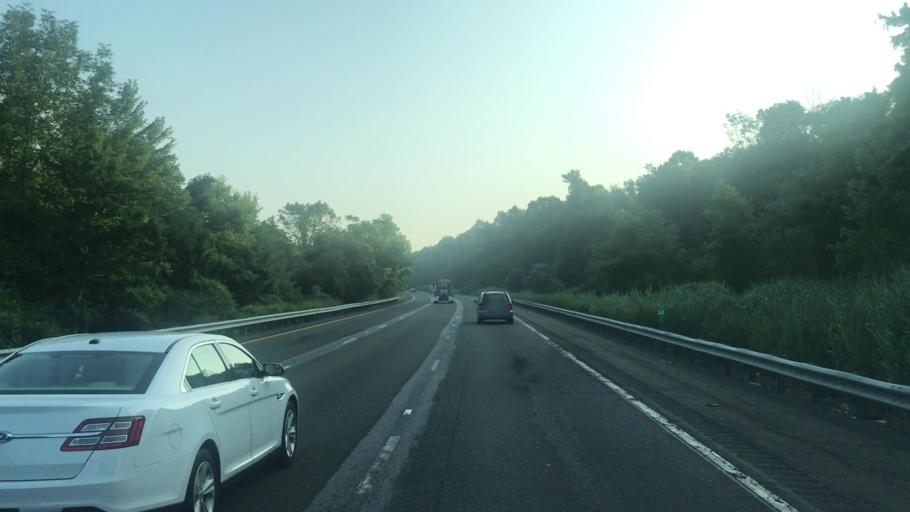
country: US
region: New York
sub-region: Westchester County
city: Armonk
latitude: 41.1543
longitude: -73.6899
